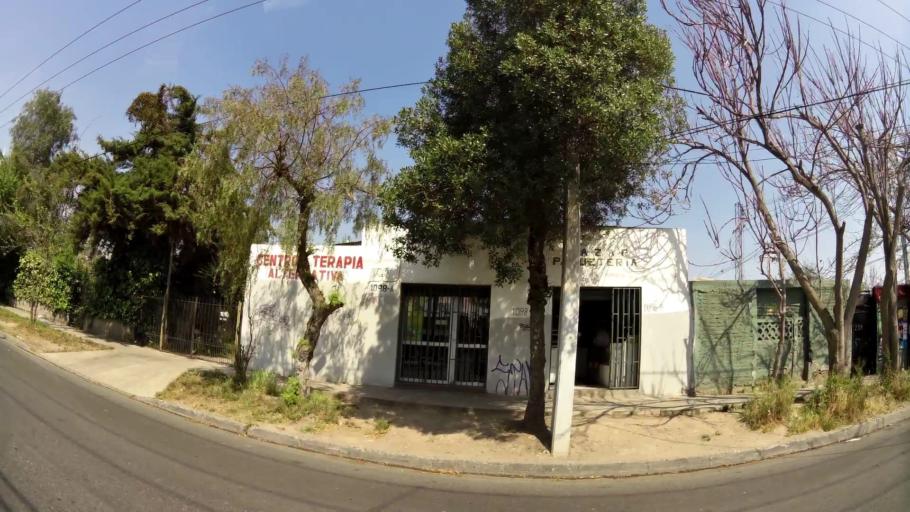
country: CL
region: Santiago Metropolitan
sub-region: Provincia de Santiago
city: La Pintana
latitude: -33.5504
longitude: -70.5991
